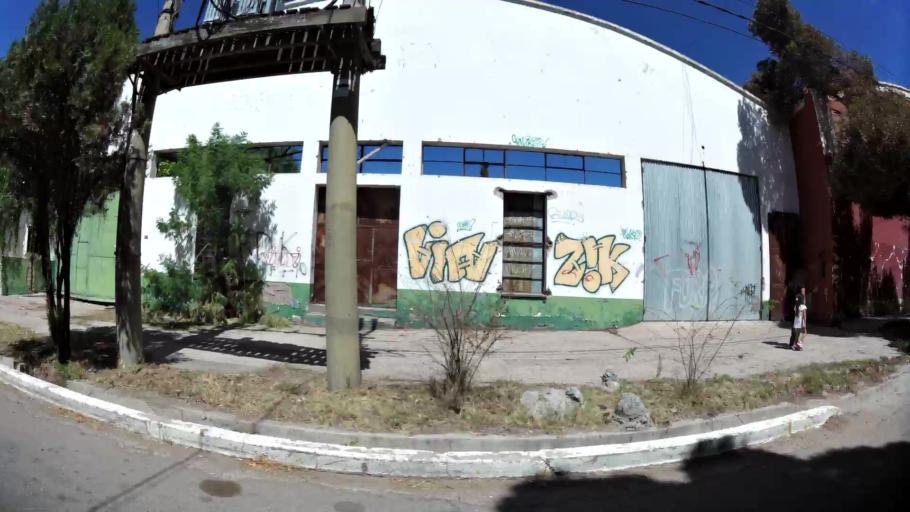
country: AR
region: Mendoza
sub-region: Departamento de Godoy Cruz
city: Godoy Cruz
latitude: -32.9617
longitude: -68.8650
